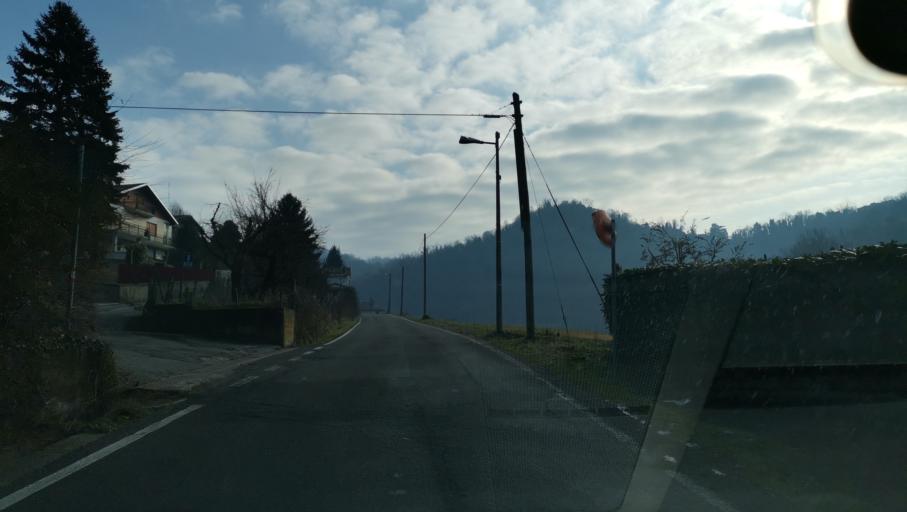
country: IT
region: Piedmont
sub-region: Provincia di Torino
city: San Raffaele Cimena
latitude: 45.1353
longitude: 7.8468
